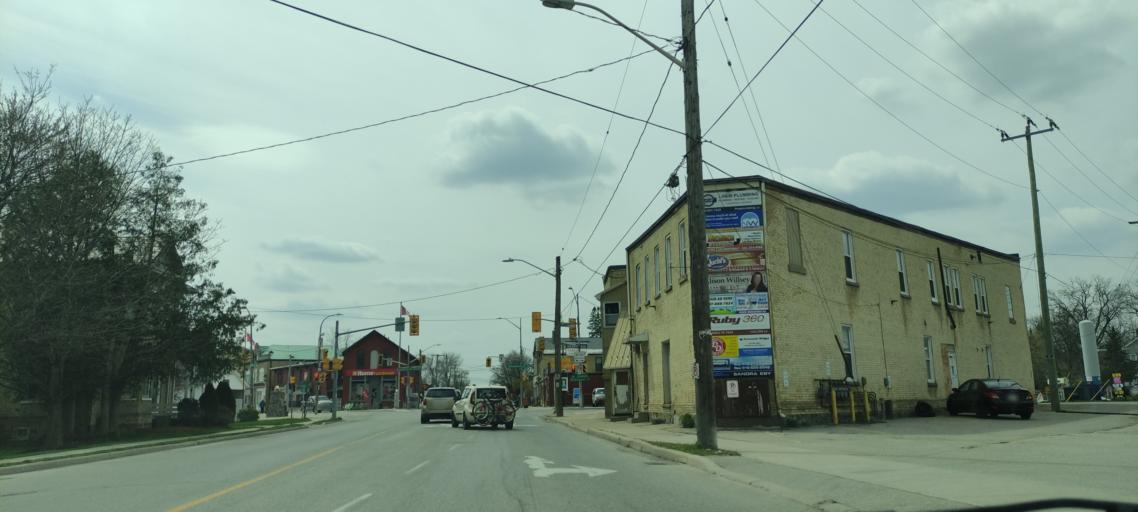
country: CA
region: Ontario
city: Stratford
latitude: 43.3212
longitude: -80.8354
